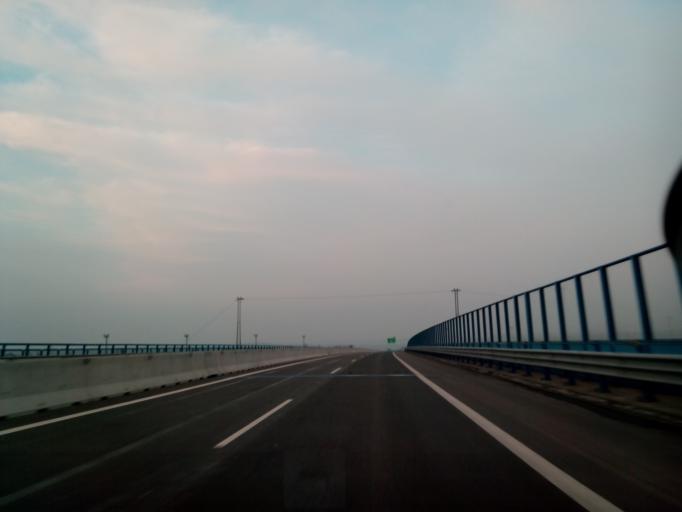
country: SK
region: Kosicky
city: Kosice
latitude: 48.6295
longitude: 21.2489
